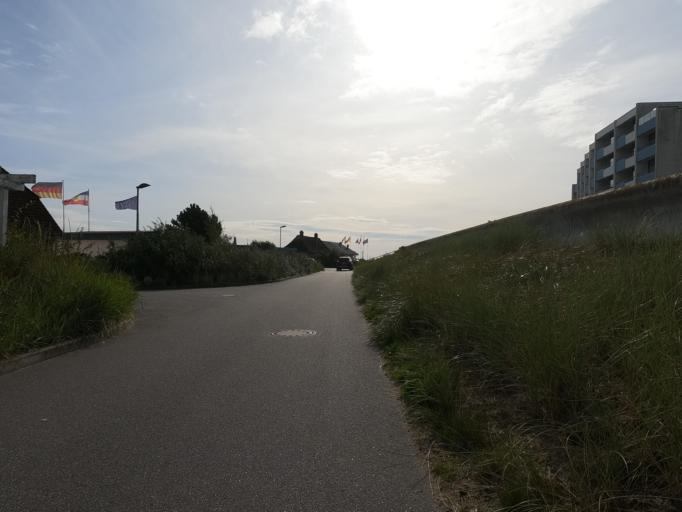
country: DE
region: Schleswig-Holstein
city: Dahme
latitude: 54.2211
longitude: 11.0885
